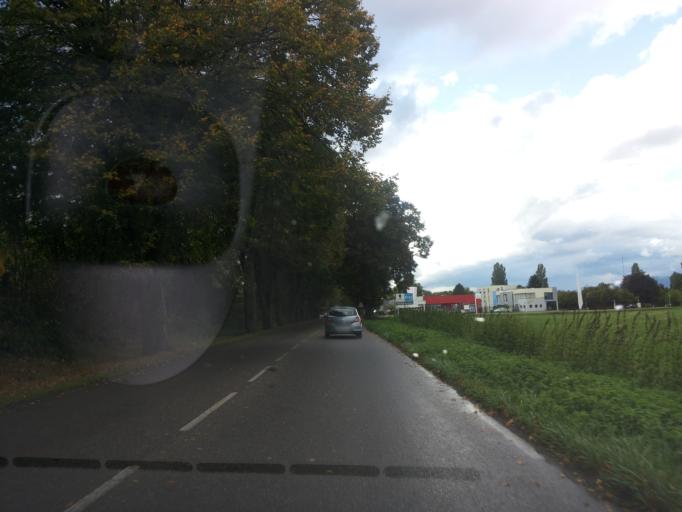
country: FR
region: Alsace
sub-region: Departement du Haut-Rhin
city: Riedisheim
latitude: 47.7563
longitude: 7.3819
